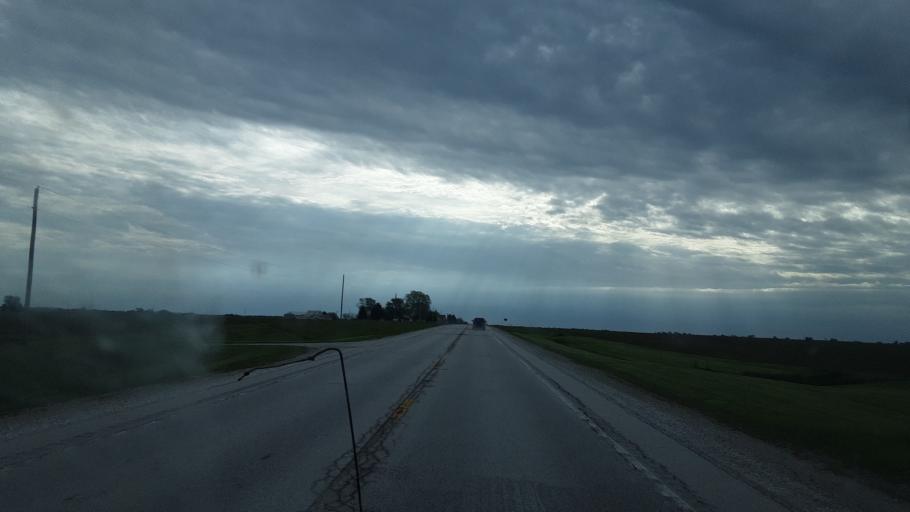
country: US
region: Illinois
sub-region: Hancock County
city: Carthage
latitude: 40.4005
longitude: -91.2042
